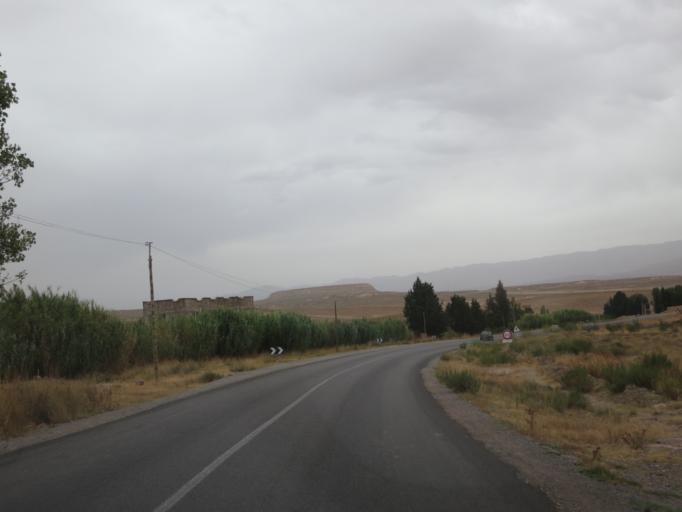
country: MA
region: Meknes-Tafilalet
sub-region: Khenifra
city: Midelt
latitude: 32.7484
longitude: -4.9146
